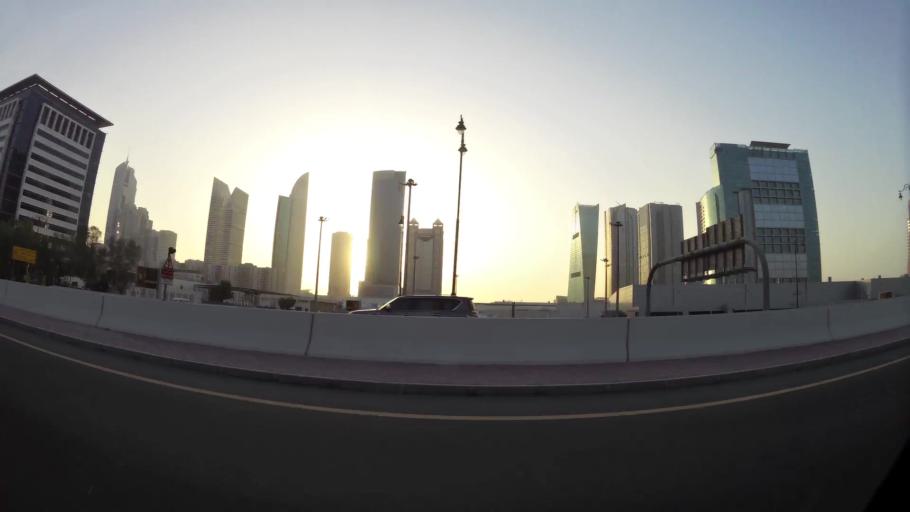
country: AE
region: Ash Shariqah
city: Sharjah
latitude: 25.2234
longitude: 55.2909
